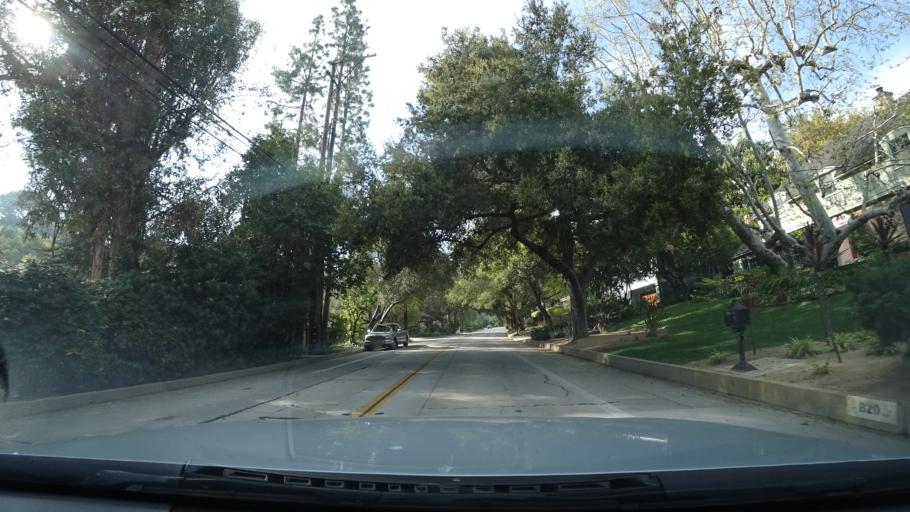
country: US
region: California
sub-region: Los Angeles County
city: South Pasadena
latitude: 34.1286
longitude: -118.1716
